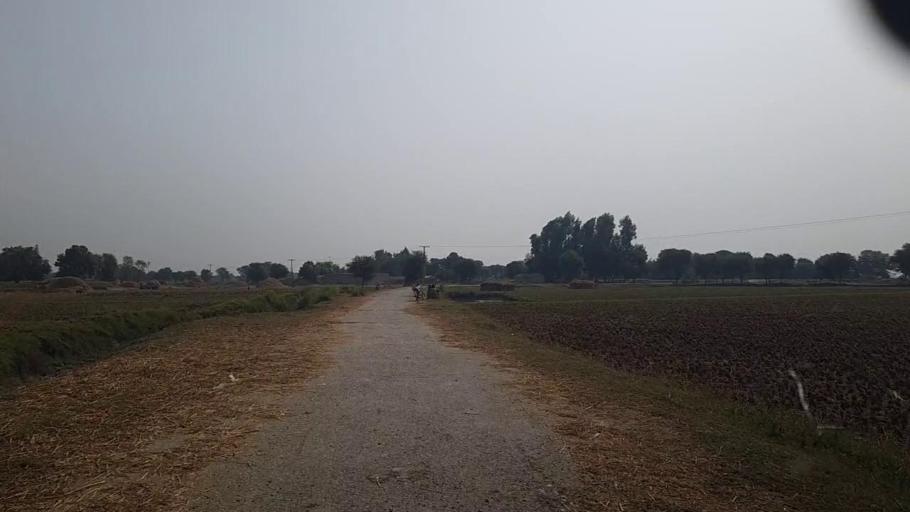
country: PK
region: Sindh
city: Kashmor
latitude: 28.3800
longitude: 69.4451
